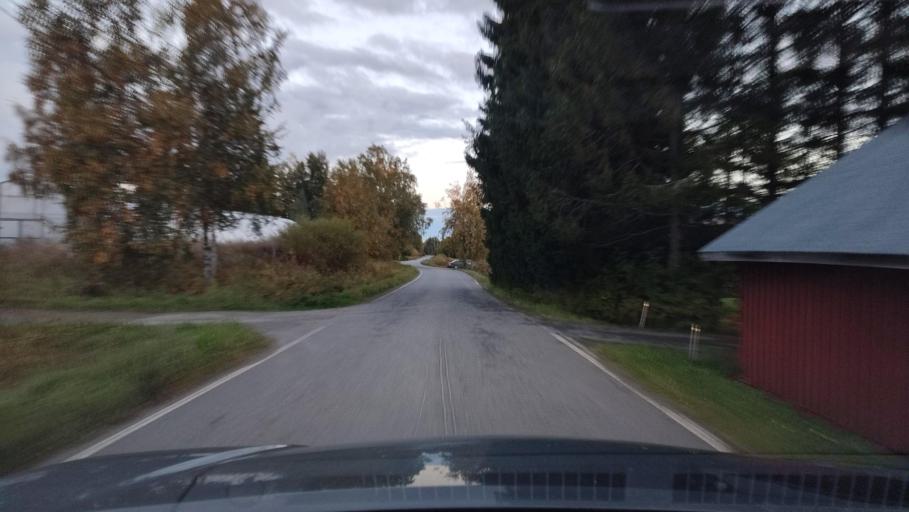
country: FI
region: Ostrobothnia
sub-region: Sydosterbotten
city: Kristinestad
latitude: 62.2705
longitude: 21.5244
